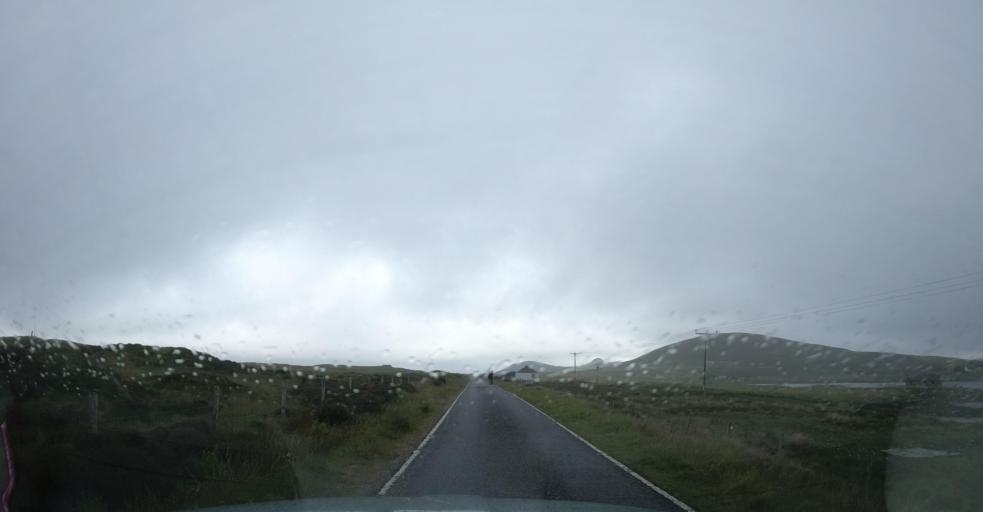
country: GB
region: Scotland
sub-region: Eilean Siar
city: Isle of North Uist
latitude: 57.6179
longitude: -7.1978
